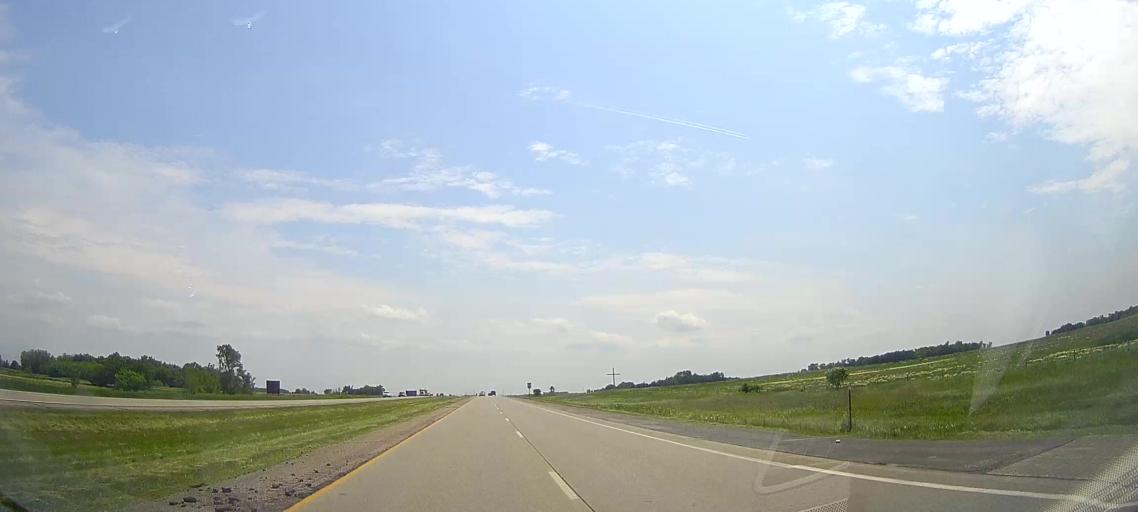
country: US
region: South Dakota
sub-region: Lincoln County
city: Tea
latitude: 43.4260
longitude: -96.7964
